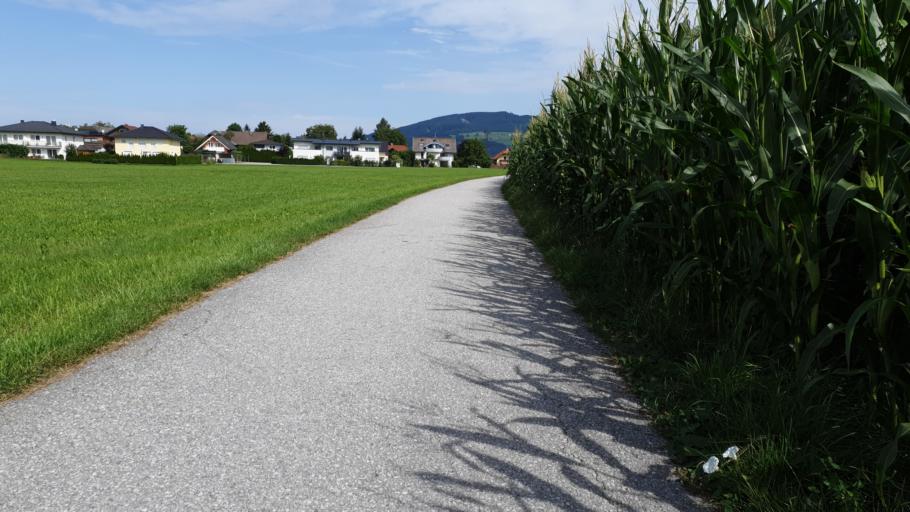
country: AT
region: Salzburg
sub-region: Politischer Bezirk Salzburg-Umgebung
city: Anthering
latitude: 47.8578
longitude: 13.0132
